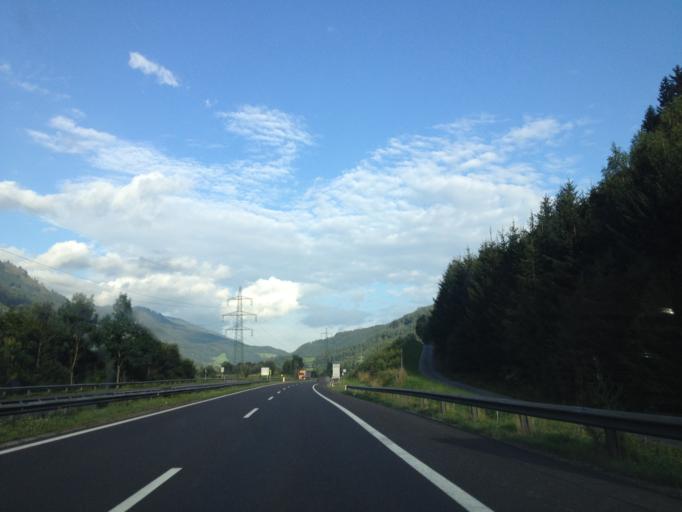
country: AT
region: Styria
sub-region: Politischer Bezirk Liezen
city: Treglwang
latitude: 47.4752
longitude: 14.5757
